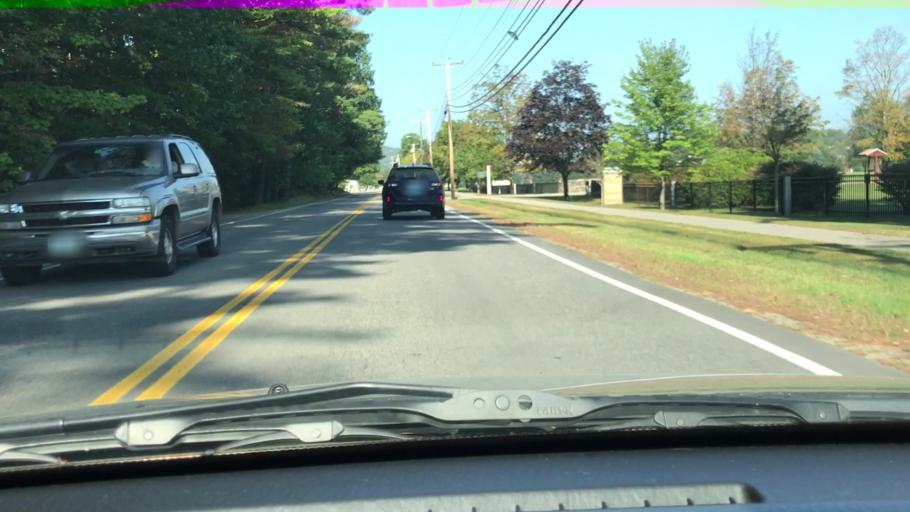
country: US
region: New Hampshire
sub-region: Cheshire County
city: Keene
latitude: 42.9458
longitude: -72.3159
